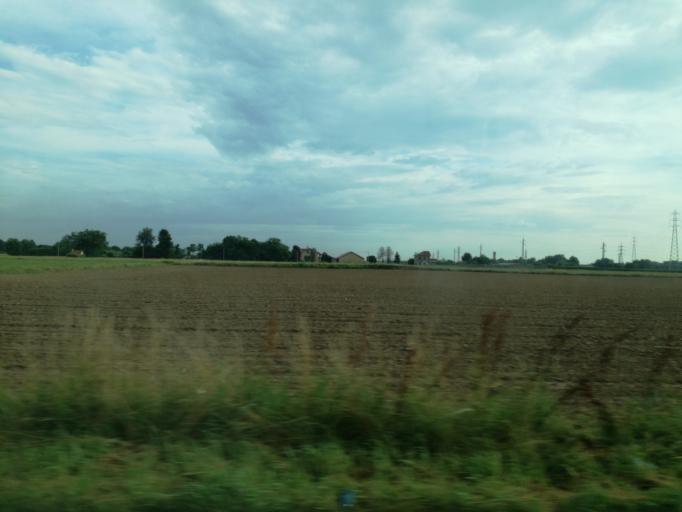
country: IT
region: Lombardy
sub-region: Provincia di Monza e Brianza
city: Velasca
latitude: 45.6220
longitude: 9.3425
